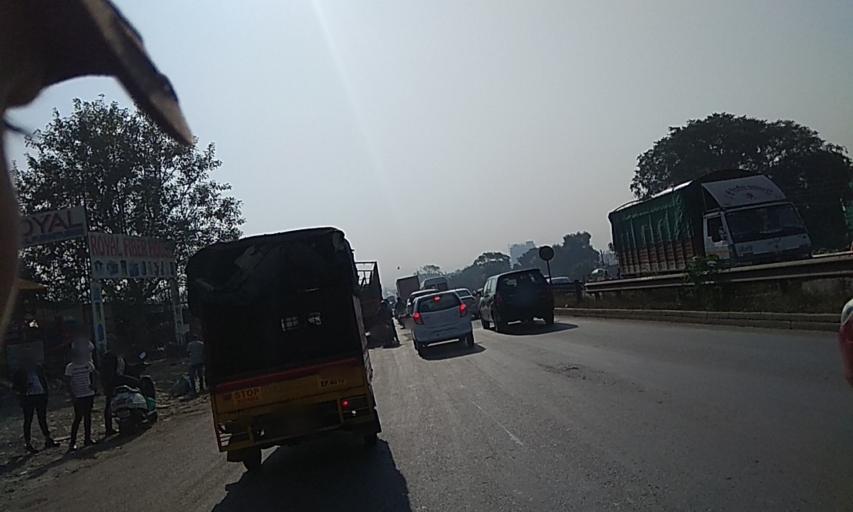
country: IN
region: Maharashtra
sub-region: Pune Division
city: Kharakvasla
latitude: 18.4775
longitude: 73.8069
